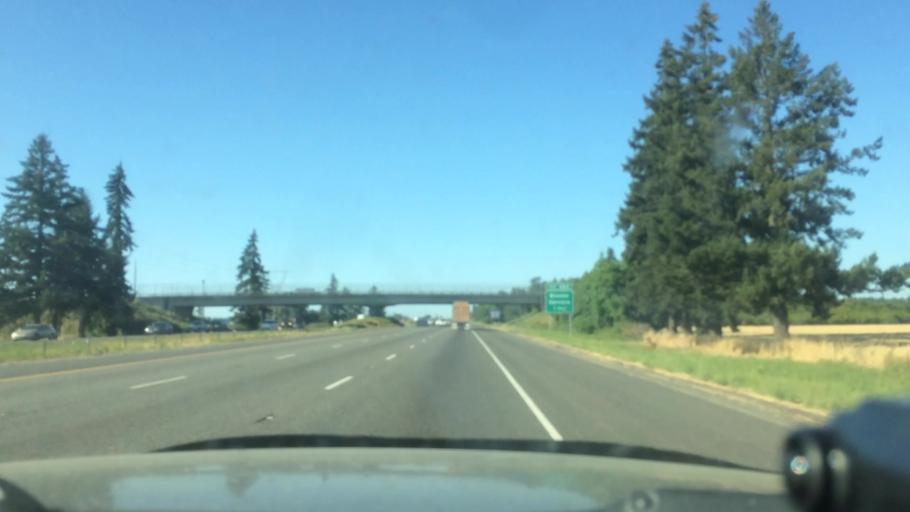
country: US
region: Oregon
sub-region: Marion County
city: Hayesville
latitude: 45.0333
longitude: -122.9813
